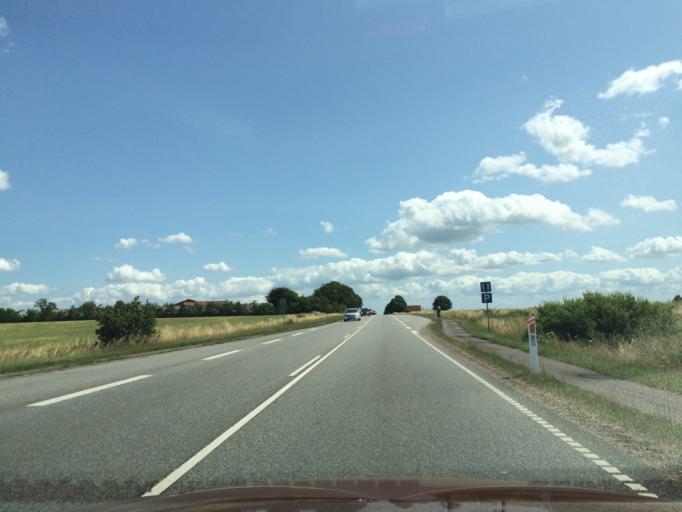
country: DK
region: Central Jutland
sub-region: Favrskov Kommune
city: Hammel
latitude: 56.2371
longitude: 9.8255
